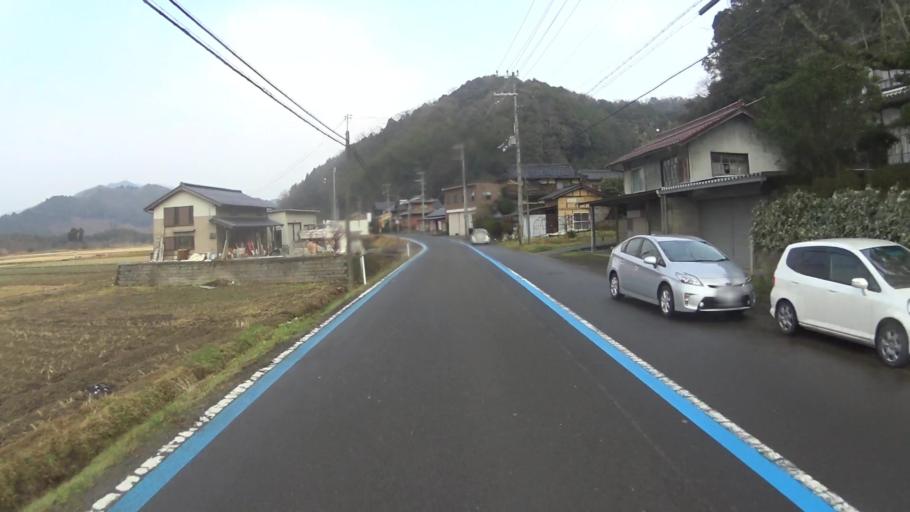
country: JP
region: Kyoto
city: Maizuru
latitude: 35.4432
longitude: 135.2651
